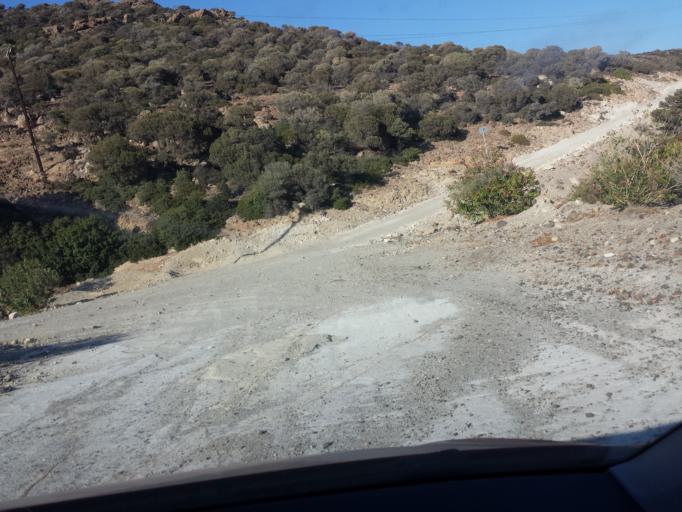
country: GR
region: South Aegean
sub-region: Nomos Kykladon
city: Milos
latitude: 36.6578
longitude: 24.3734
